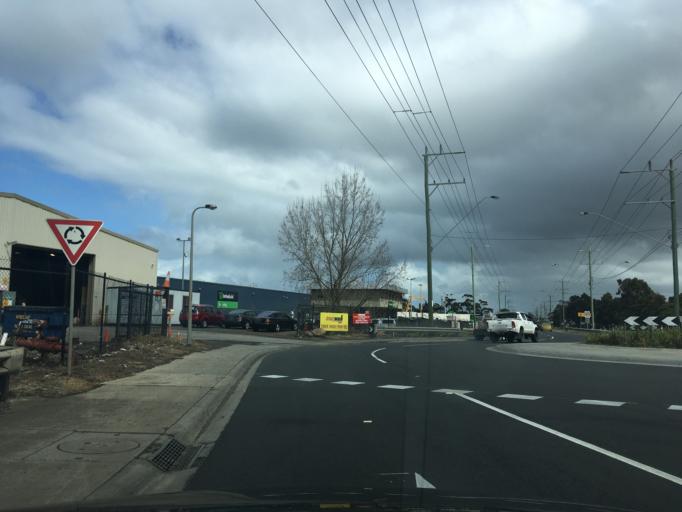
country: AU
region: Victoria
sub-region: Hobsons Bay
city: Laverton
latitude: -37.8323
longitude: 144.7847
